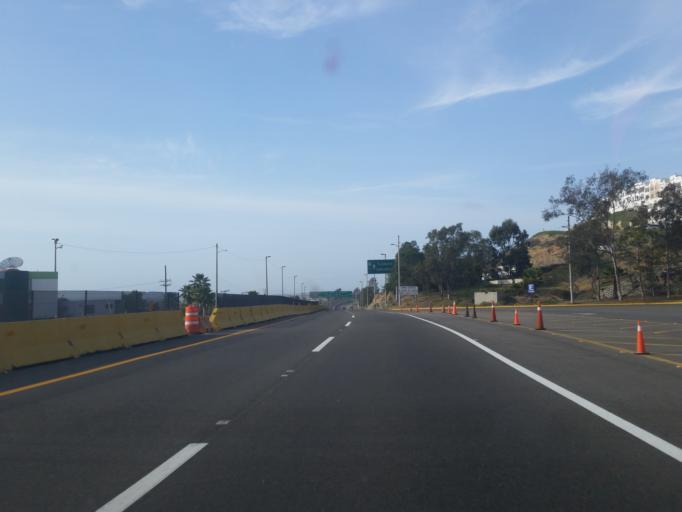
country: US
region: California
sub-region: San Diego County
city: Imperial Beach
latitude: 32.5263
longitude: -117.1077
